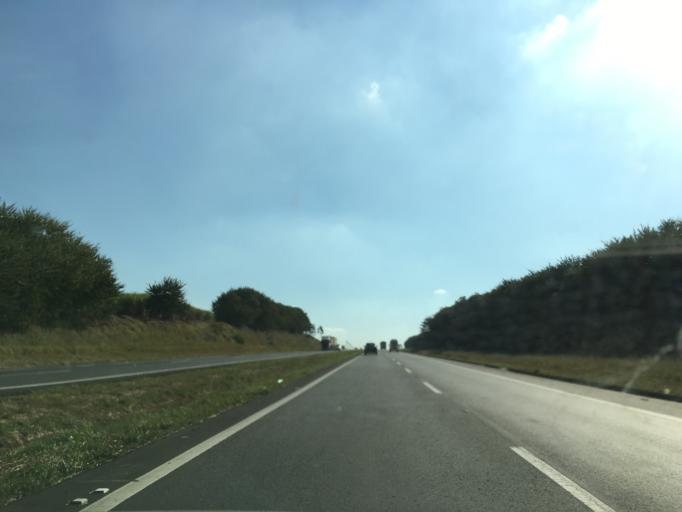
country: BR
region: Sao Paulo
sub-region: Piracicaba
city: Piracicaba
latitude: -22.7260
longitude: -47.5640
